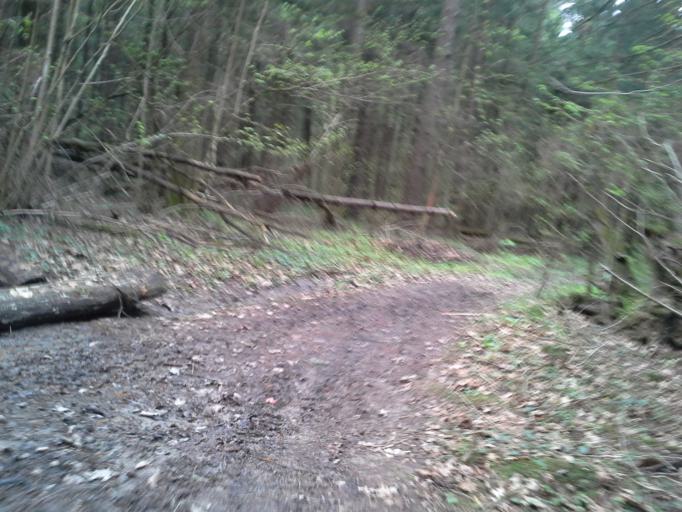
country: RU
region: Moskovskaya
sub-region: Leninskiy Rayon
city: Vnukovo
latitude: 55.6403
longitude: 37.2955
